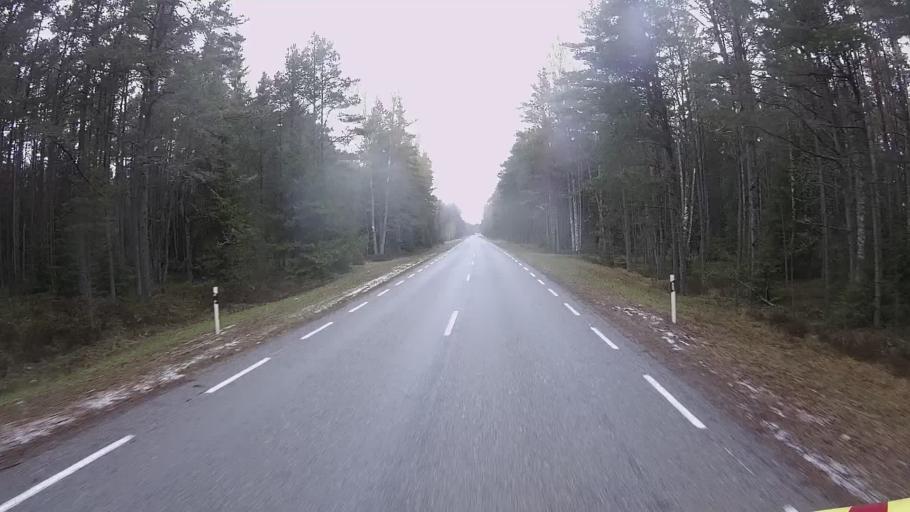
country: EE
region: Hiiumaa
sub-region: Kaerdla linn
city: Kardla
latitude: 59.0620
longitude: 22.6853
